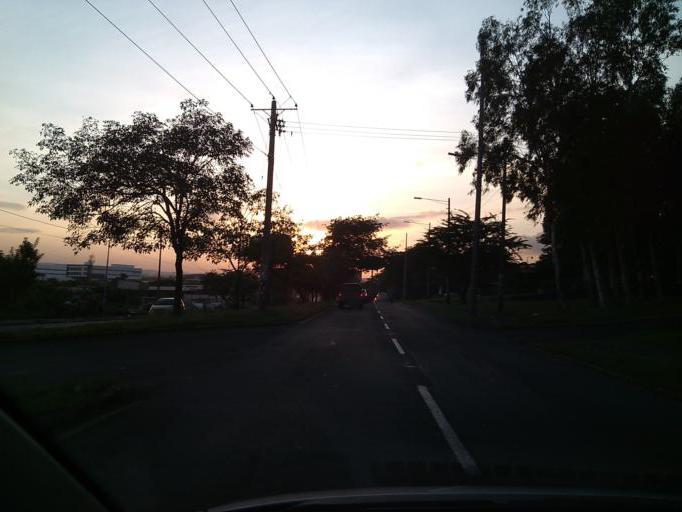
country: NI
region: Managua
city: Managua
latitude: 12.1368
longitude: -86.2731
